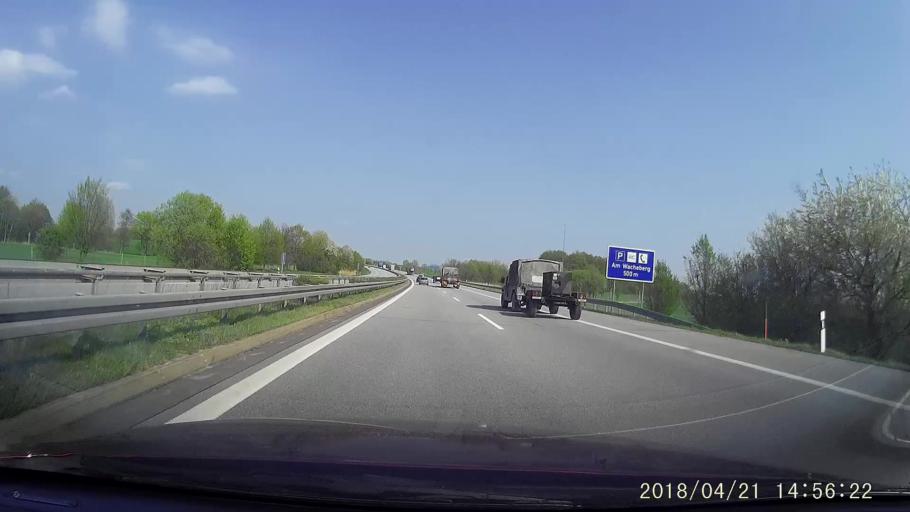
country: DE
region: Saxony
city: Weissenberg
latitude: 51.2059
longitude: 14.6720
